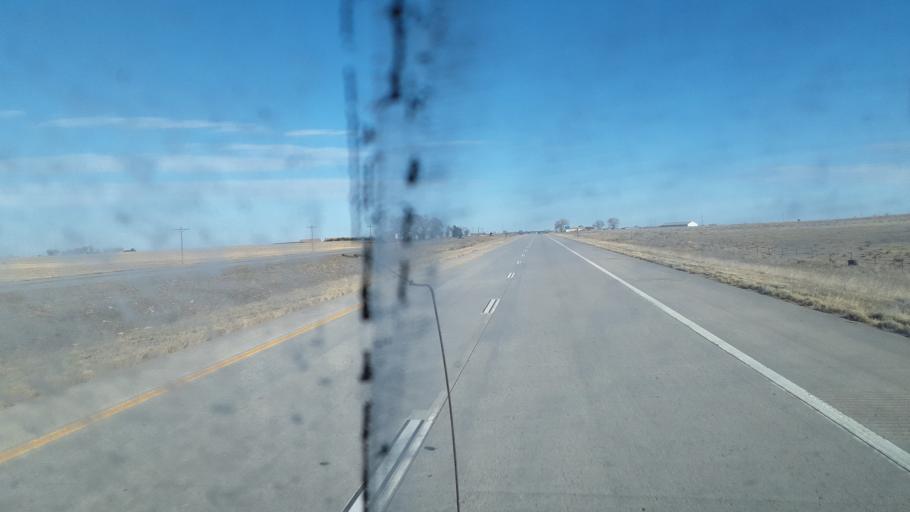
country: US
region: Colorado
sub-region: Morgan County
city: Fort Morgan
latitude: 40.2322
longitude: -104.1121
